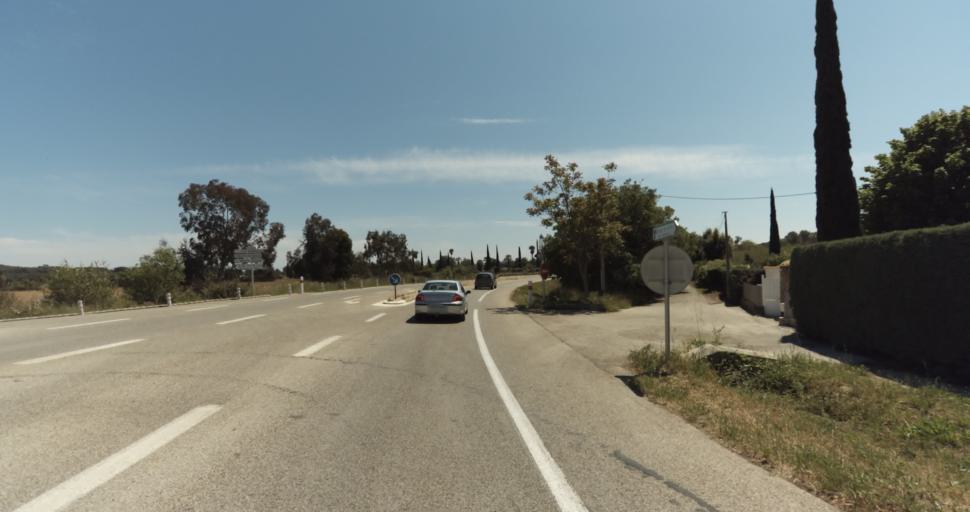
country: FR
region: Provence-Alpes-Cote d'Azur
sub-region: Departement du Var
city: Hyeres
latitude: 43.1445
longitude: 6.1533
